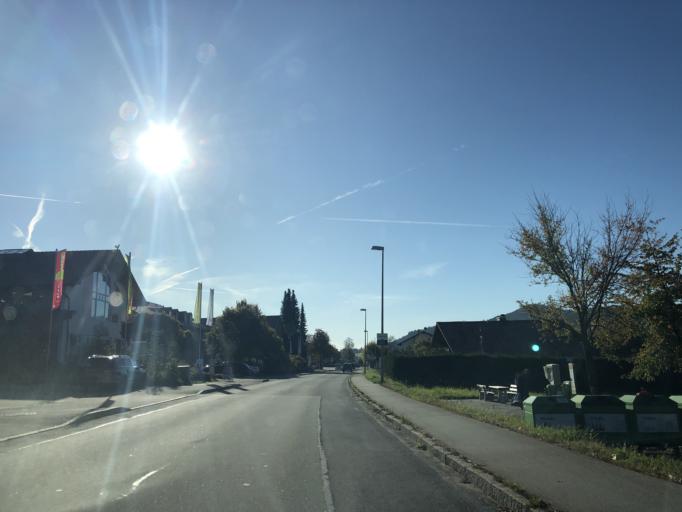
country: DE
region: Bavaria
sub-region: Lower Bavaria
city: Bodenmais
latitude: 49.0714
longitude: 13.0931
